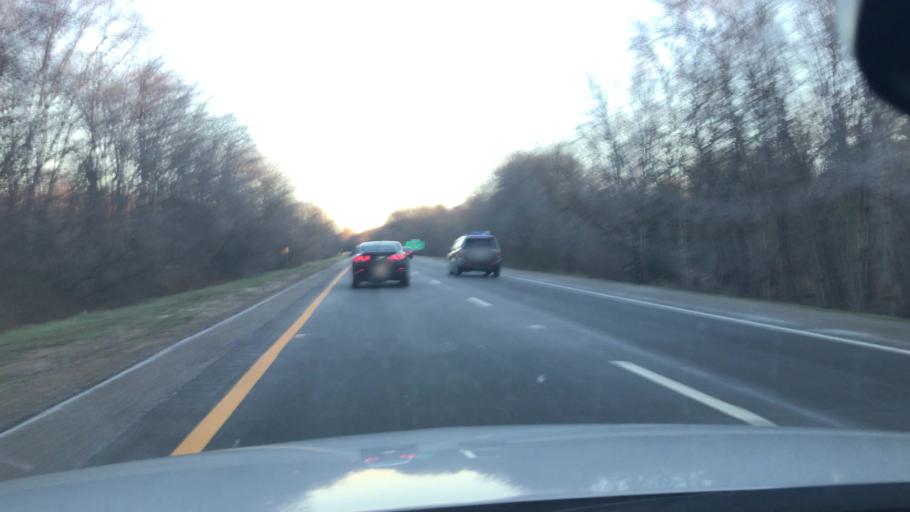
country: US
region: New Jersey
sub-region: Camden County
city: Sicklerville
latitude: 39.7237
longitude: -74.9995
